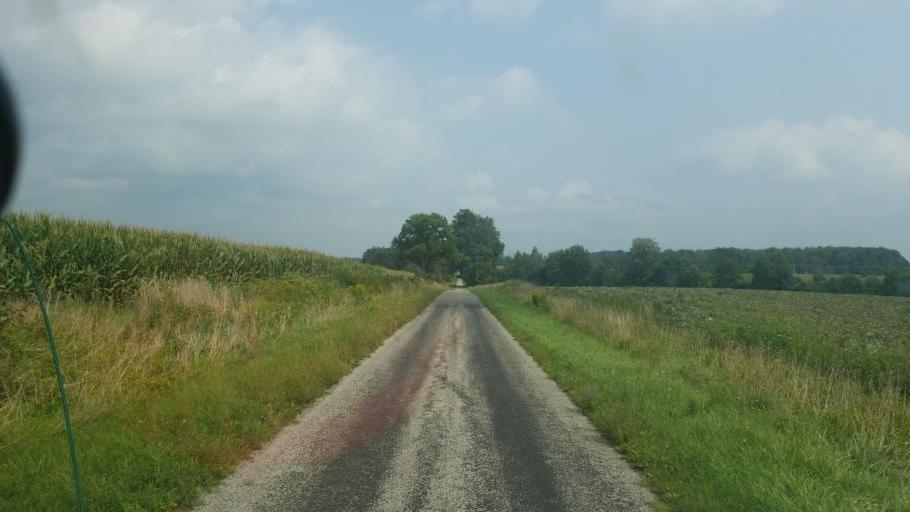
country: US
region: Ohio
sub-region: Huron County
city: Greenwich
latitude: 41.0907
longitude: -82.5699
